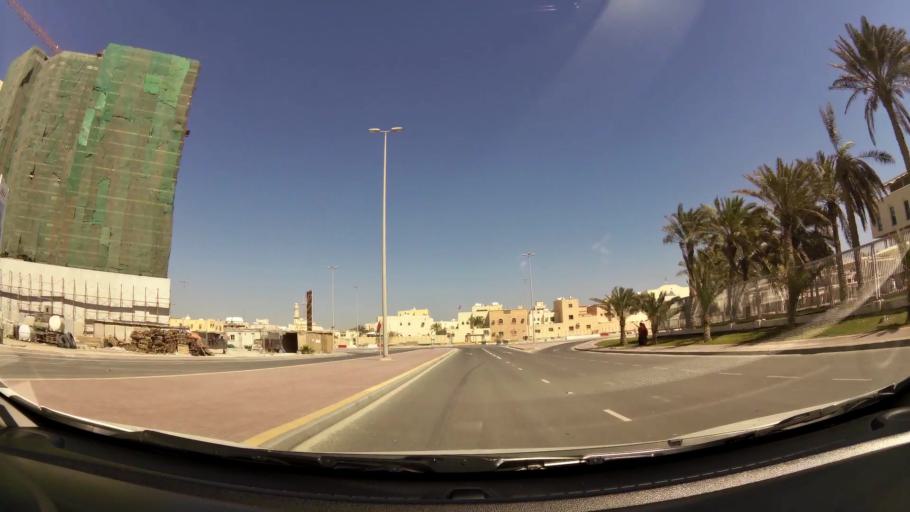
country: BH
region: Muharraq
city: Al Muharraq
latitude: 26.2658
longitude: 50.5979
